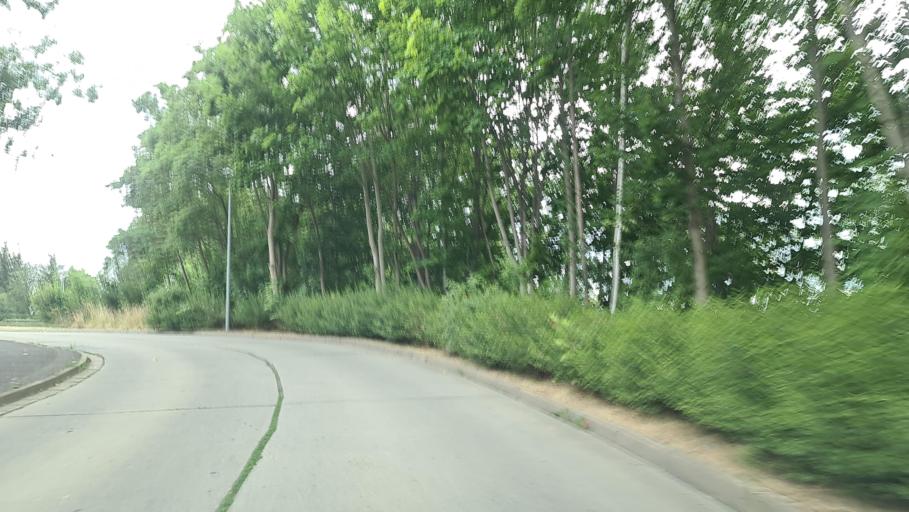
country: DE
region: Saxony
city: Plauen
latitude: 50.4980
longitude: 12.1586
